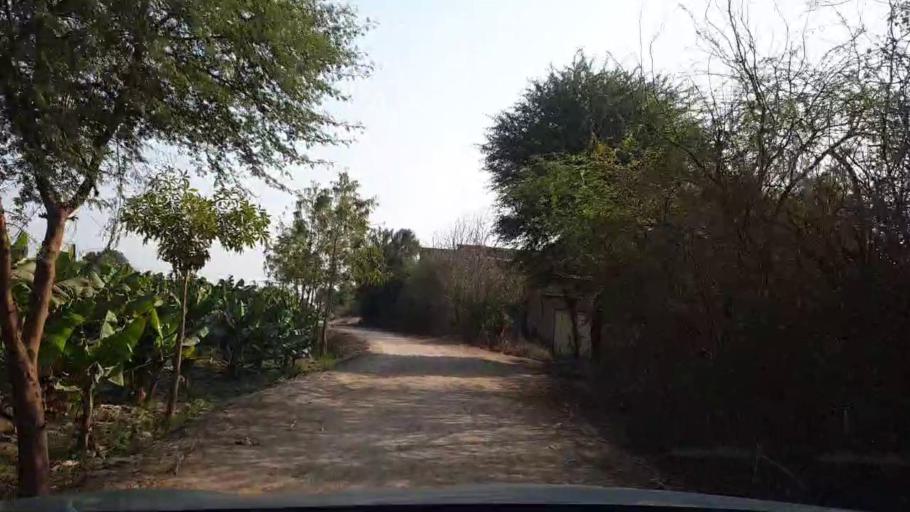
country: PK
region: Sindh
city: Tando Allahyar
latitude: 25.5534
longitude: 68.7875
